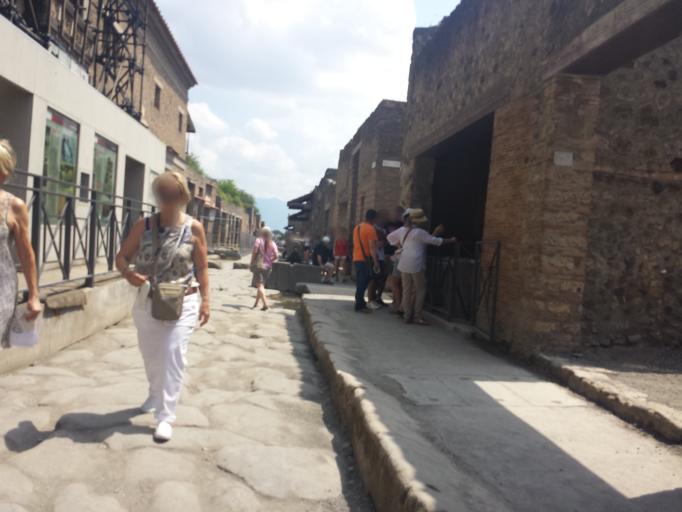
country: IT
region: Campania
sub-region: Provincia di Napoli
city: Pompei
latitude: 40.7508
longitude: 14.4901
